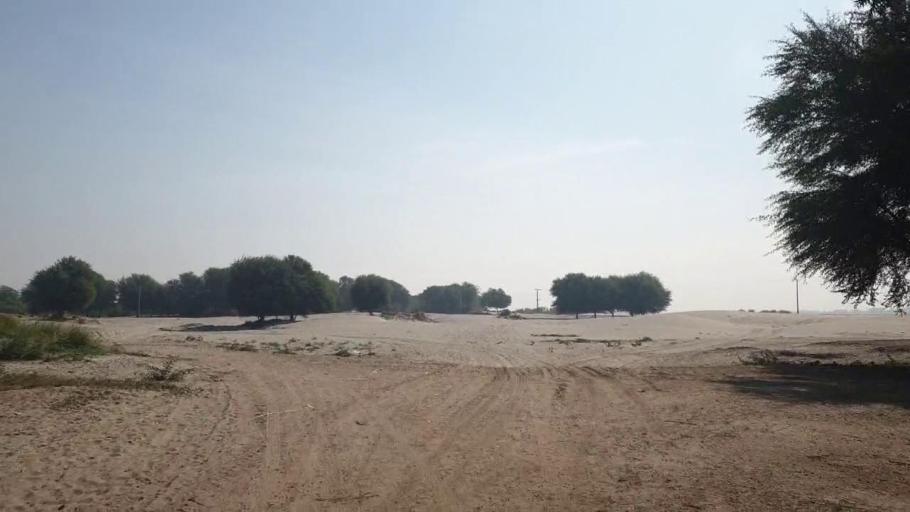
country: PK
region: Sindh
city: Matiari
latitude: 25.6733
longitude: 68.3624
